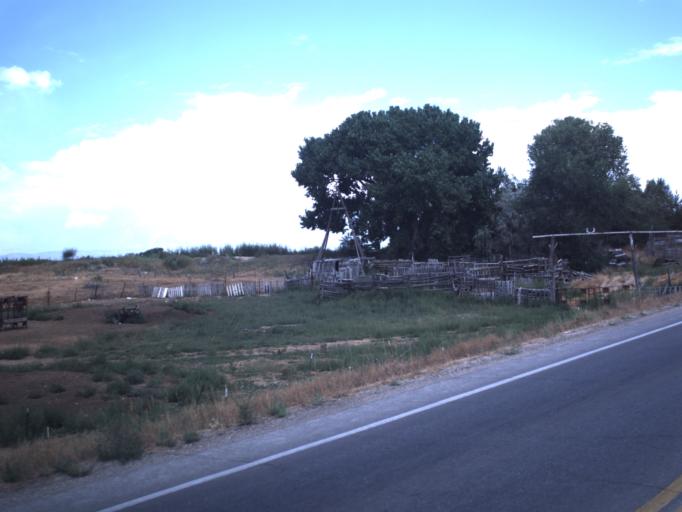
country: US
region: Utah
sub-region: Uintah County
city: Naples
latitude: 40.4096
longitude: -109.4990
